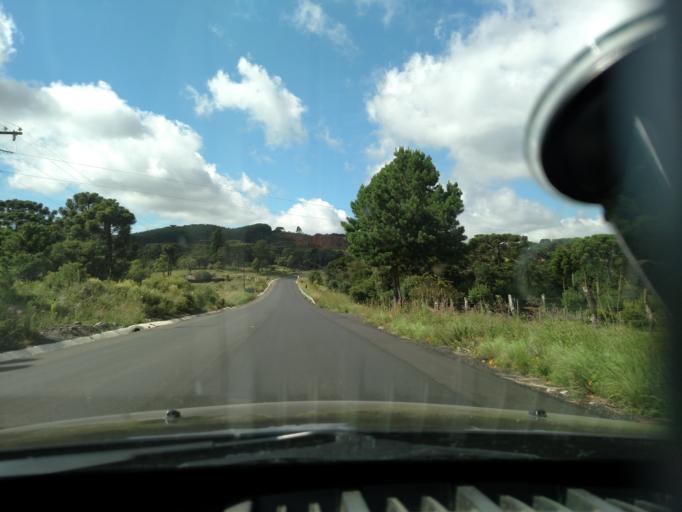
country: BR
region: Santa Catarina
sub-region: Lages
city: Lages
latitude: -27.9359
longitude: -50.0946
